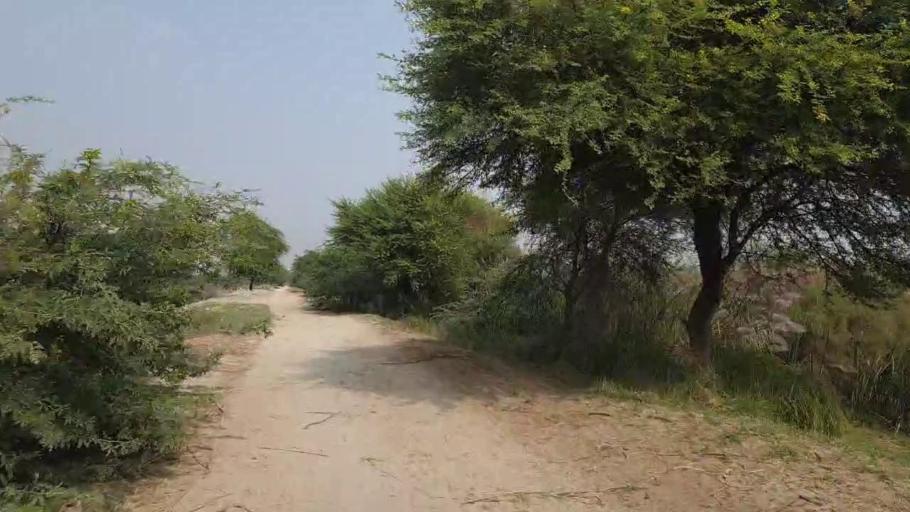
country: PK
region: Sindh
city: Kario
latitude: 24.7636
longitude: 68.5241
